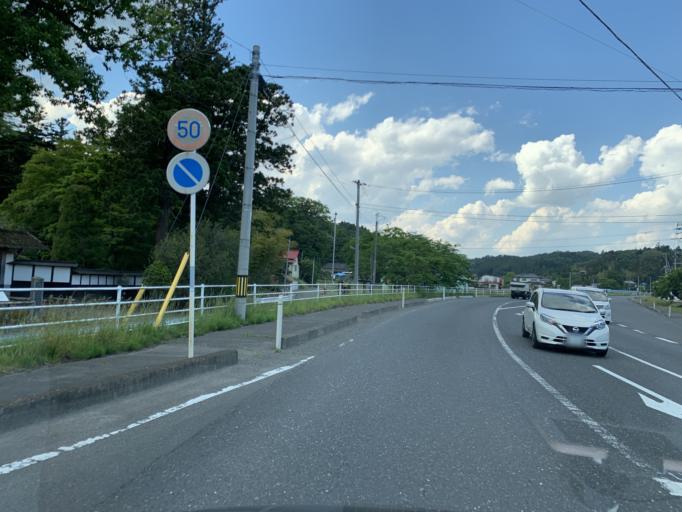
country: JP
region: Miyagi
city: Wakuya
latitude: 38.5462
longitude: 141.1410
